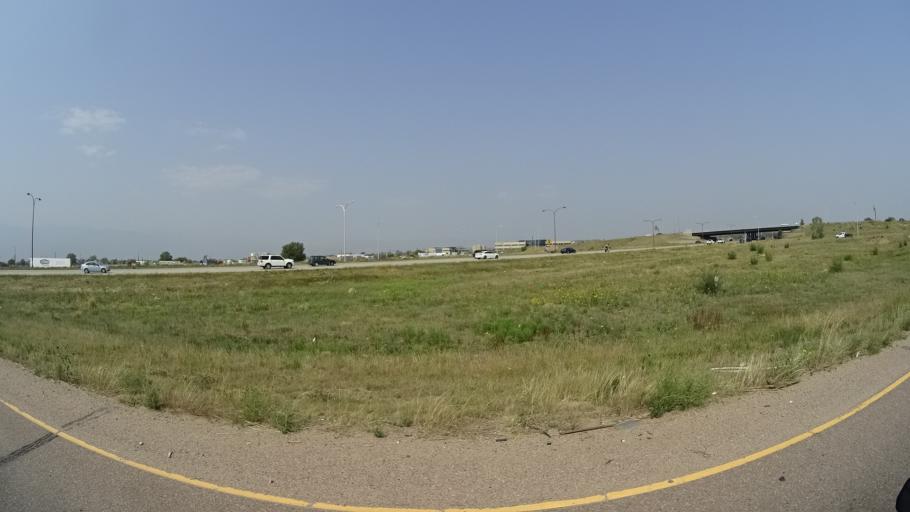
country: US
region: Colorado
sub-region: El Paso County
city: Cimarron Hills
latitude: 38.8362
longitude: -104.7201
